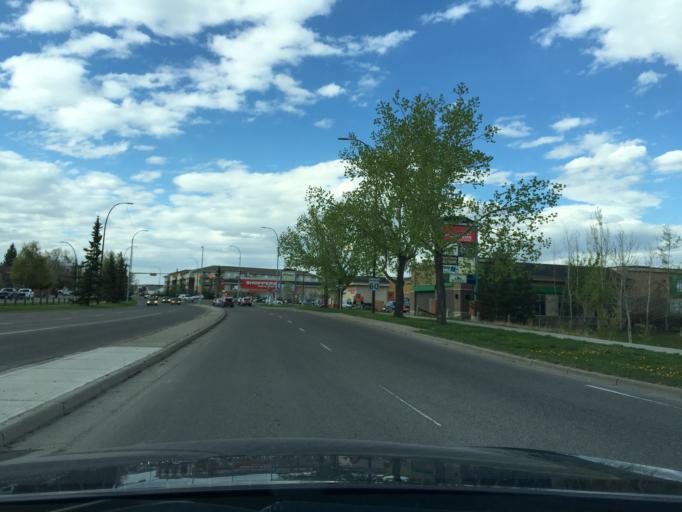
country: CA
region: Alberta
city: Calgary
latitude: 50.9131
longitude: -114.0737
